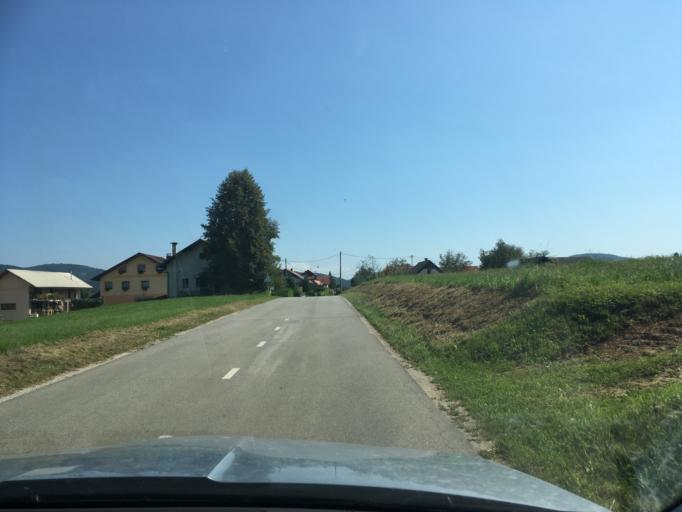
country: SI
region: Metlika
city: Metlika
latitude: 45.5709
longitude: 15.2932
